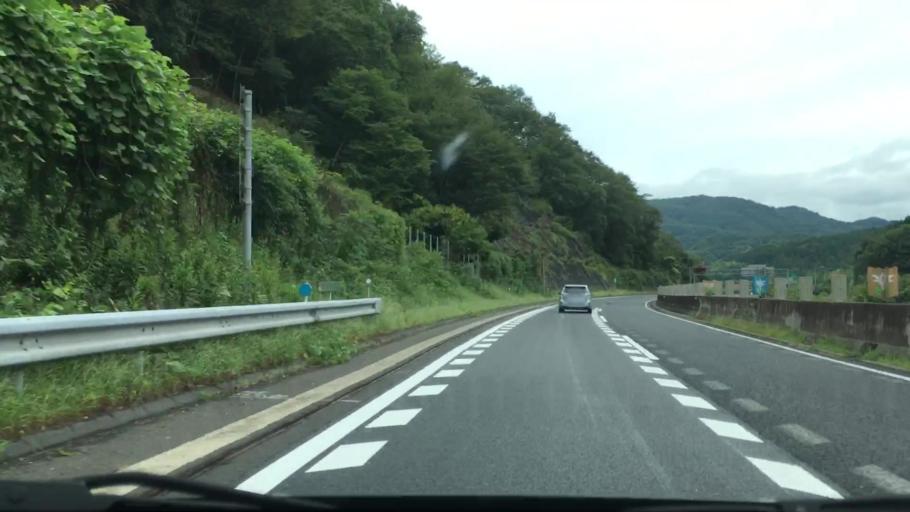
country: JP
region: Hyogo
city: Yamazakicho-nakabirose
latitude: 35.0198
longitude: 134.3781
